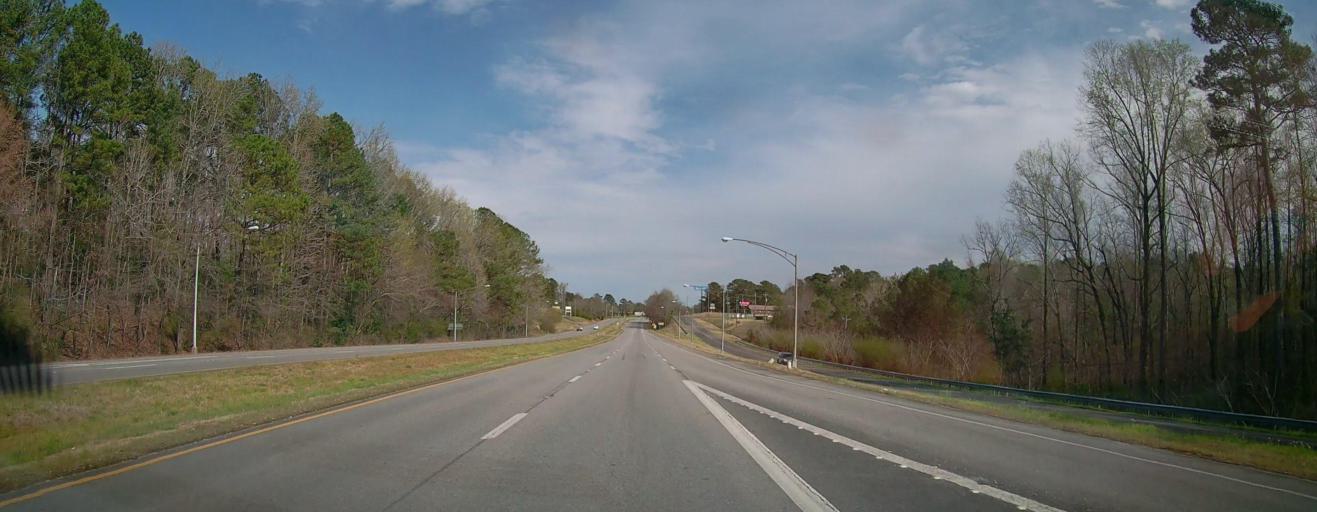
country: US
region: Alabama
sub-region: Jefferson County
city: Adamsville
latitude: 33.5842
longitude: -86.9290
